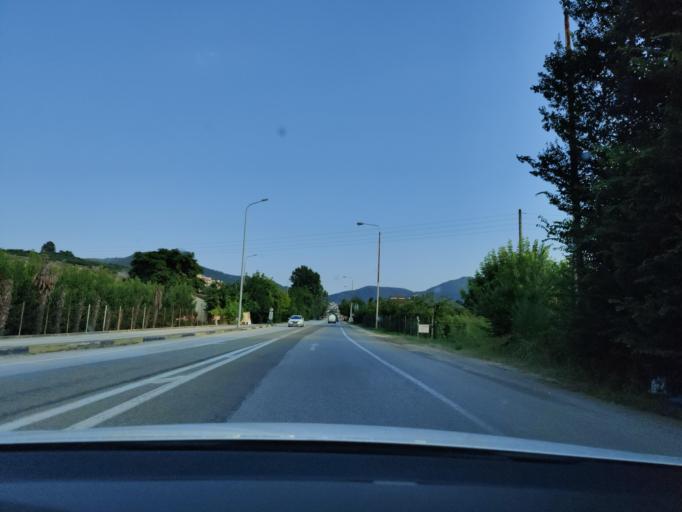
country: GR
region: East Macedonia and Thrace
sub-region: Nomos Kavalas
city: Amygdaleonas
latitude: 40.9692
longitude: 24.3532
